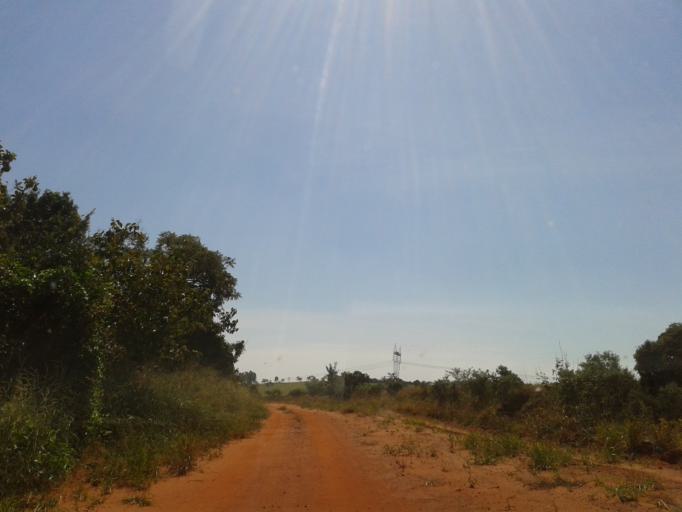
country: BR
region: Minas Gerais
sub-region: Campina Verde
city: Campina Verde
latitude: -19.4504
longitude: -49.5641
